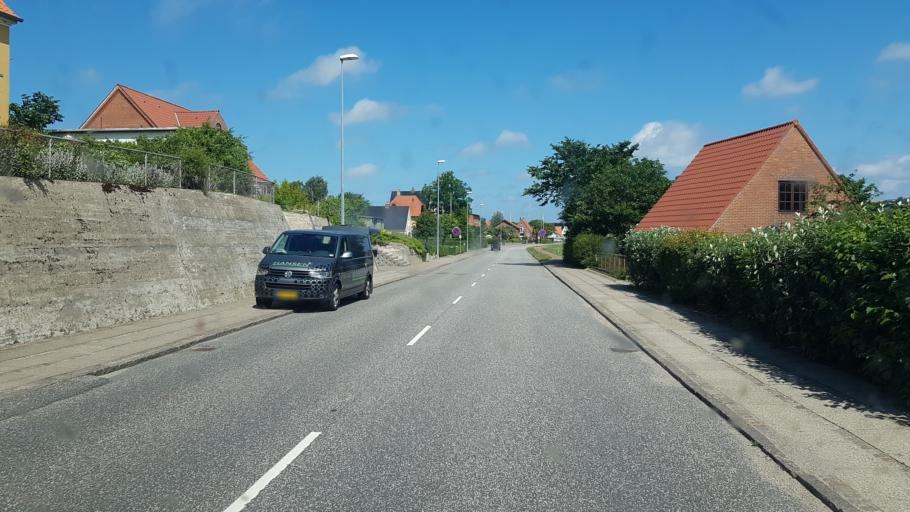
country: DK
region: Central Jutland
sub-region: Lemvig Kommune
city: Lemvig
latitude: 56.5437
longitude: 8.3141
